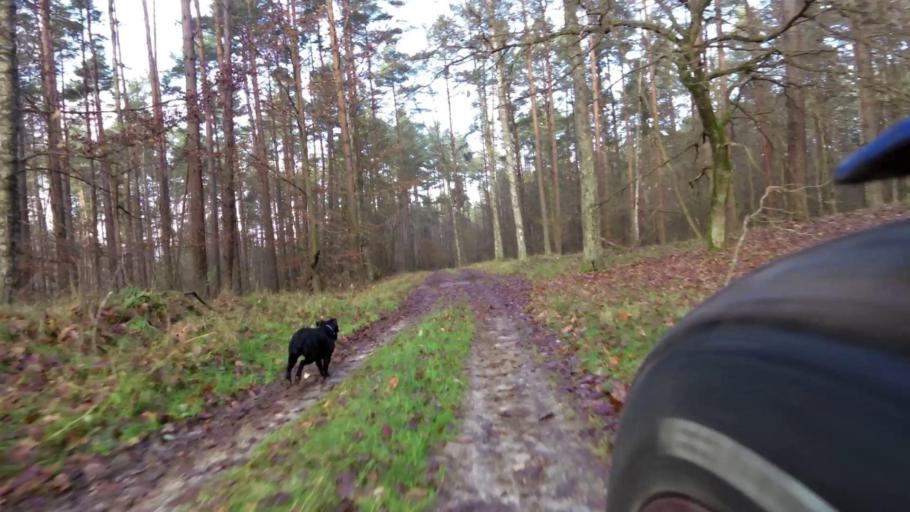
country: PL
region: West Pomeranian Voivodeship
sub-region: Powiat szczecinecki
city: Borne Sulinowo
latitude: 53.6079
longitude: 16.6172
